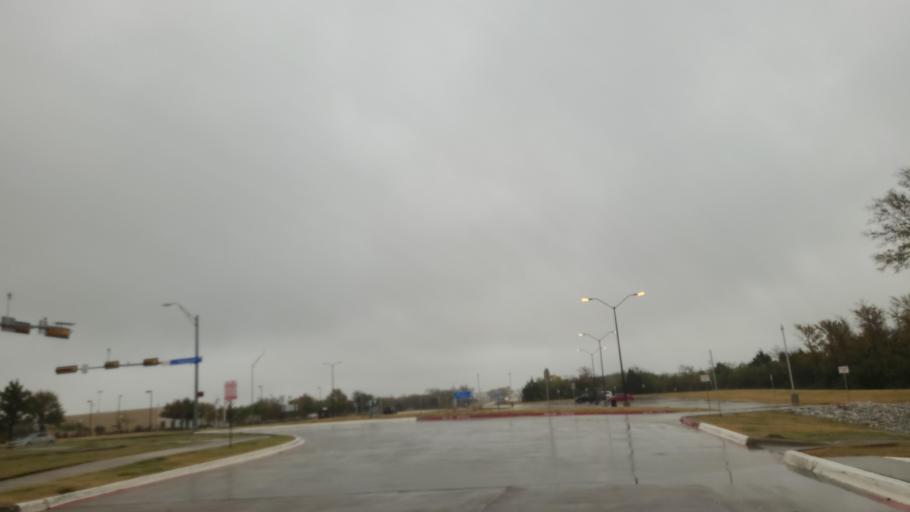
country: US
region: Texas
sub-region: Tarrant County
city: Euless
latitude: 32.8525
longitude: -97.0386
